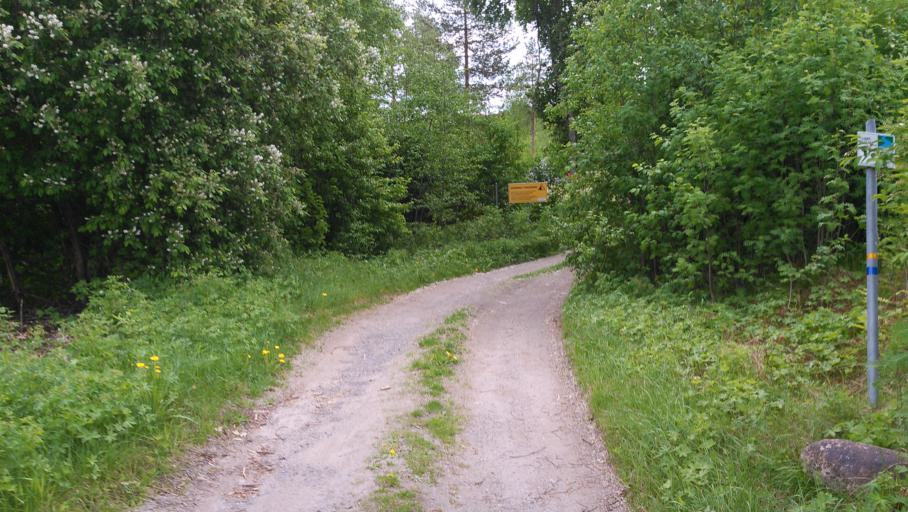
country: SE
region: Vaesterbotten
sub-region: Umea Kommun
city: Roback
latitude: 63.8805
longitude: 20.0239
